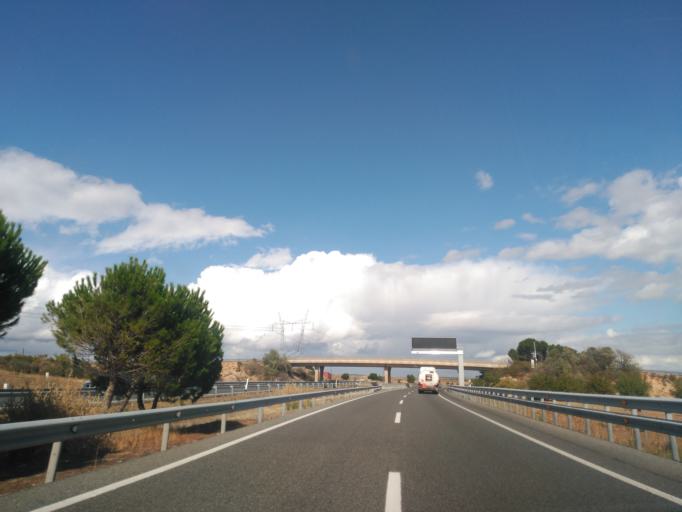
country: ES
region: Castille and Leon
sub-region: Provincia de Burgos
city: Celada del Camino
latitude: 42.2618
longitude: -3.9411
